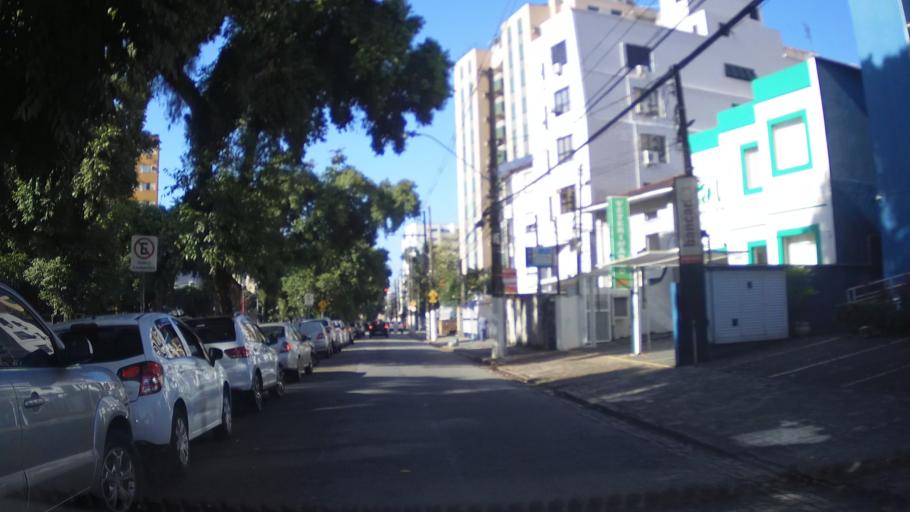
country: BR
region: Sao Paulo
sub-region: Santos
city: Santos
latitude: -23.9524
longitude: -46.3261
